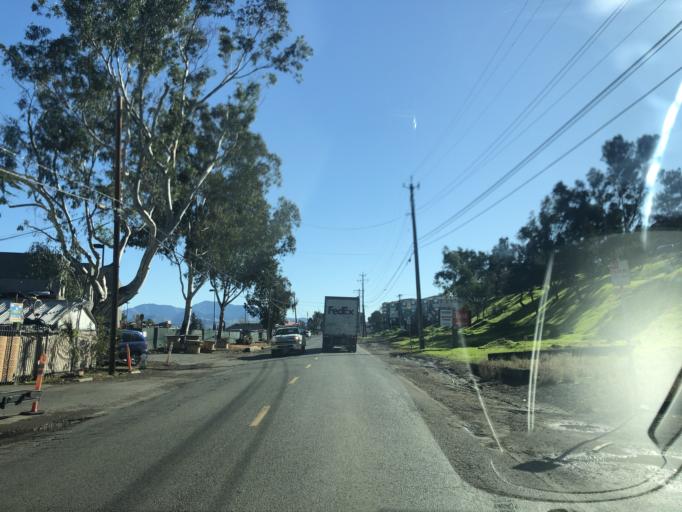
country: US
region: California
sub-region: Contra Costa County
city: Pacheco
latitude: 37.9993
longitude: -122.0787
